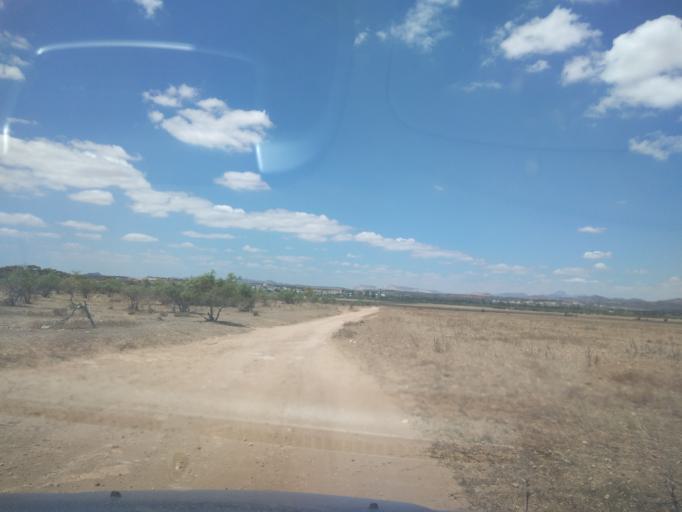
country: TN
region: Susah
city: Harqalah
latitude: 36.1675
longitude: 10.4383
